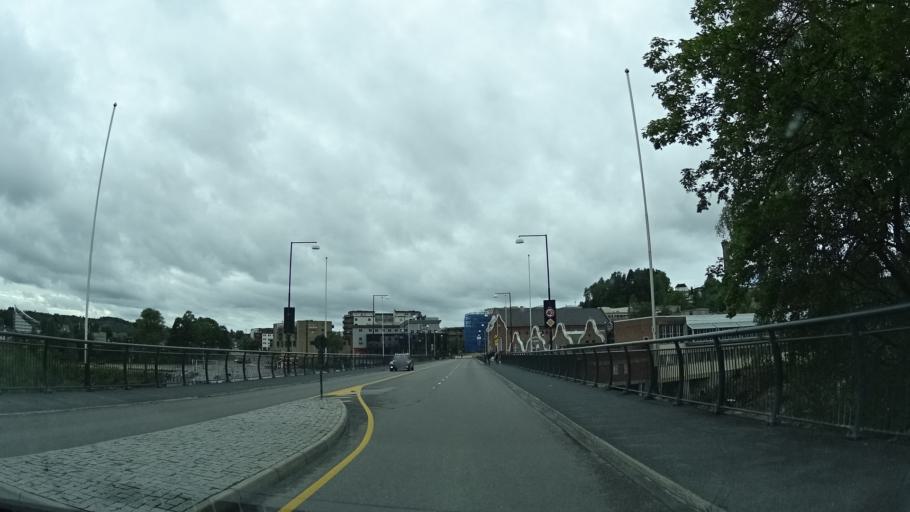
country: NO
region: Buskerud
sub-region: Ringerike
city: Honefoss
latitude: 60.1700
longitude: 10.2581
